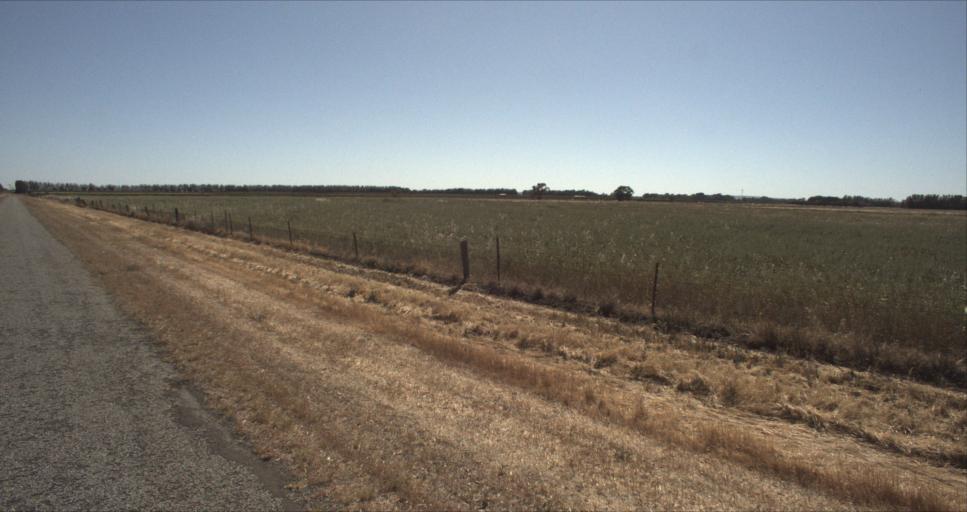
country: AU
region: New South Wales
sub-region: Leeton
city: Leeton
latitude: -34.5357
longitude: 146.3174
